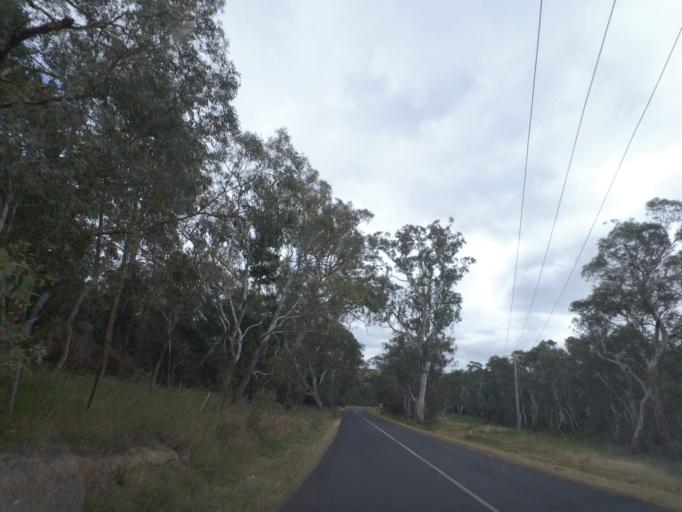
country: AU
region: Victoria
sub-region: Whittlesea
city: Whittlesea
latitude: -37.1997
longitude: 145.0401
